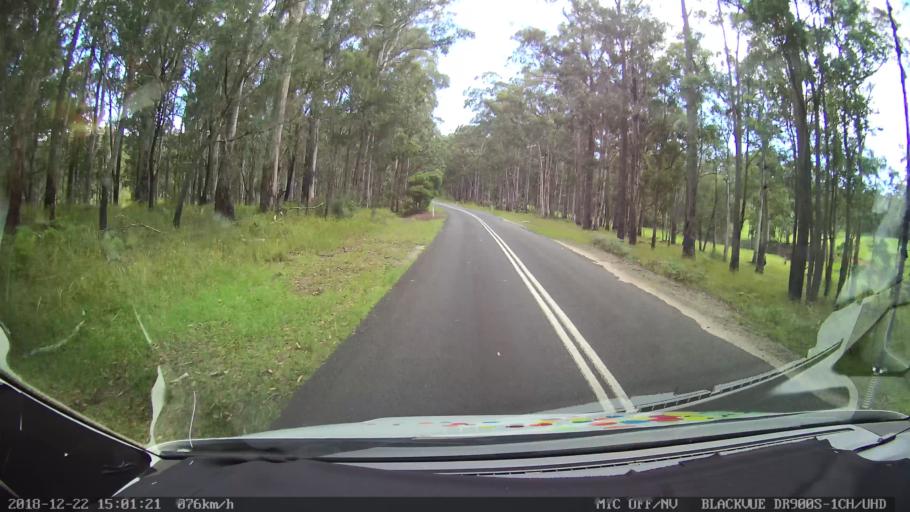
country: AU
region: New South Wales
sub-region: Bellingen
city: Dorrigo
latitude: -30.2536
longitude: 152.4592
